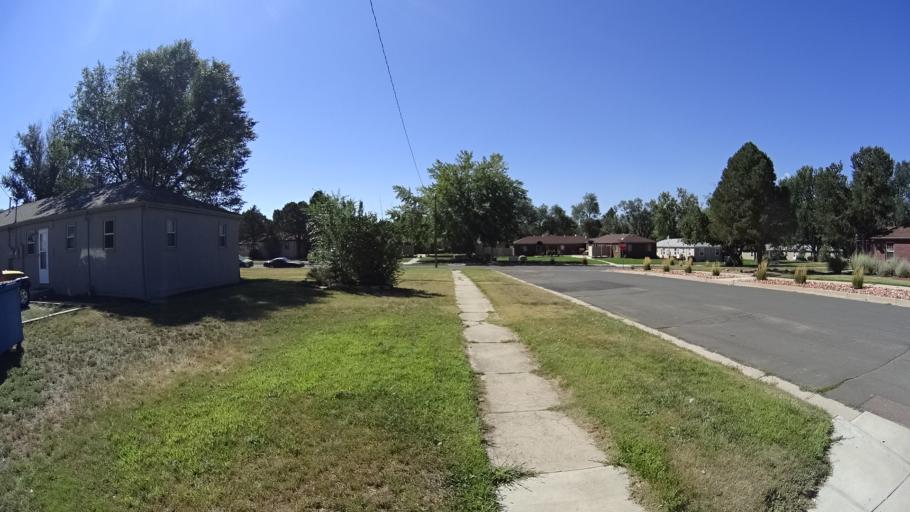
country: US
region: Colorado
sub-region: El Paso County
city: Colorado Springs
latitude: 38.8549
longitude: -104.7986
